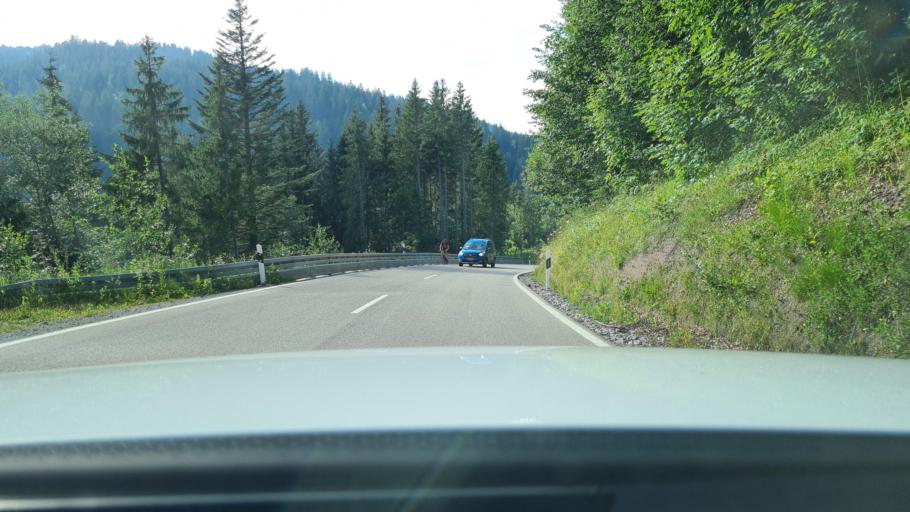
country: DE
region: Bavaria
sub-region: Swabia
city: Balderschwang
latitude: 47.4395
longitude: 10.1422
